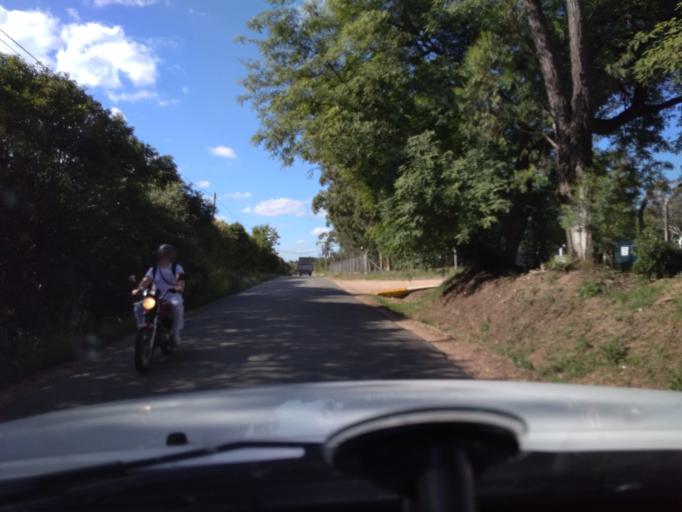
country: UY
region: Canelones
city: La Paz
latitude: -34.7958
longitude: -56.2113
